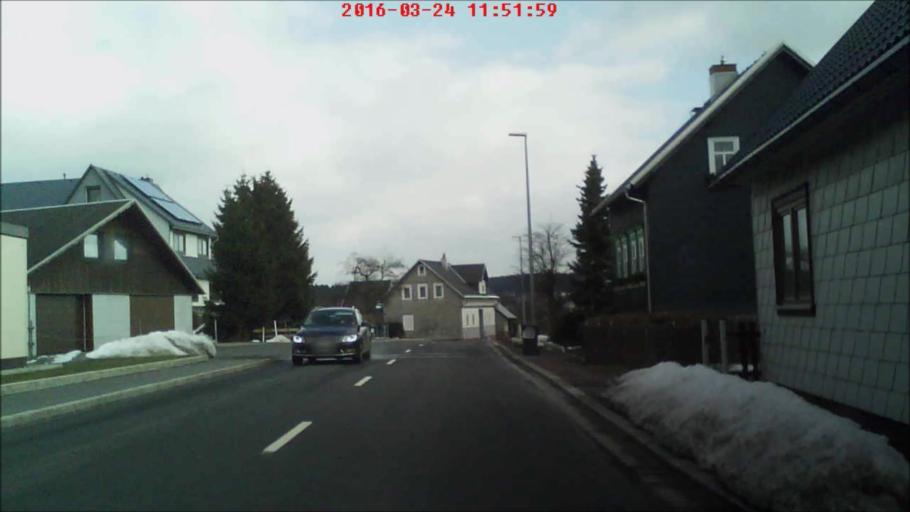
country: DE
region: Thuringia
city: Steinheid
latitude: 50.4714
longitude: 11.0534
